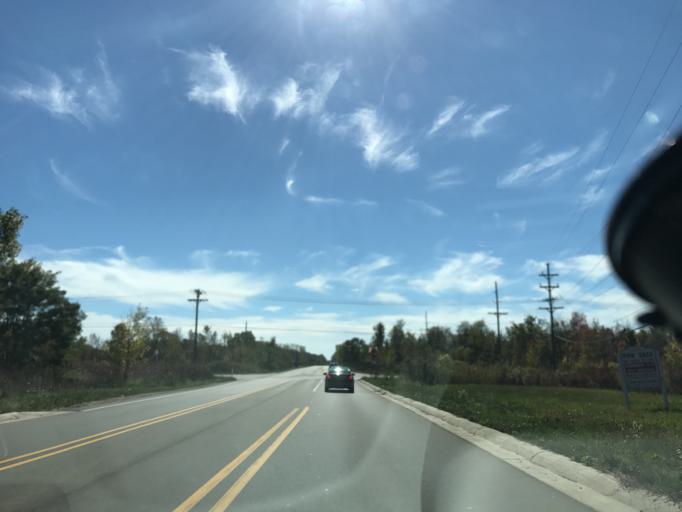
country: US
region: Michigan
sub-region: Oakland County
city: South Lyon
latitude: 42.4478
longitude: -83.6309
